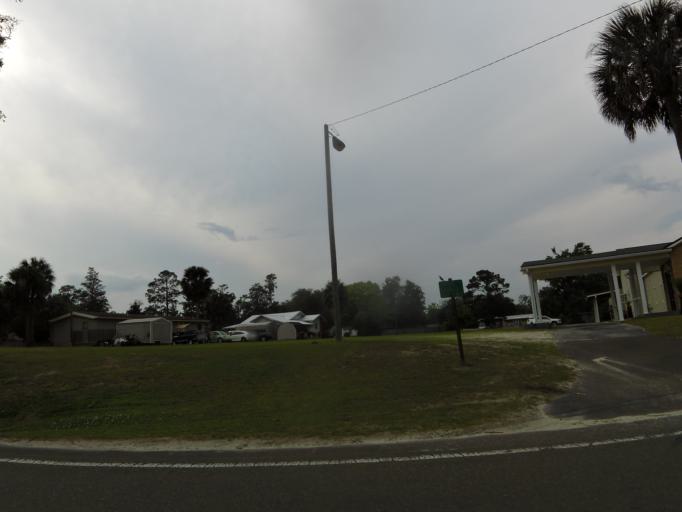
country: US
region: Florida
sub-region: Nassau County
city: Hilliard
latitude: 30.6922
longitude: -81.9161
